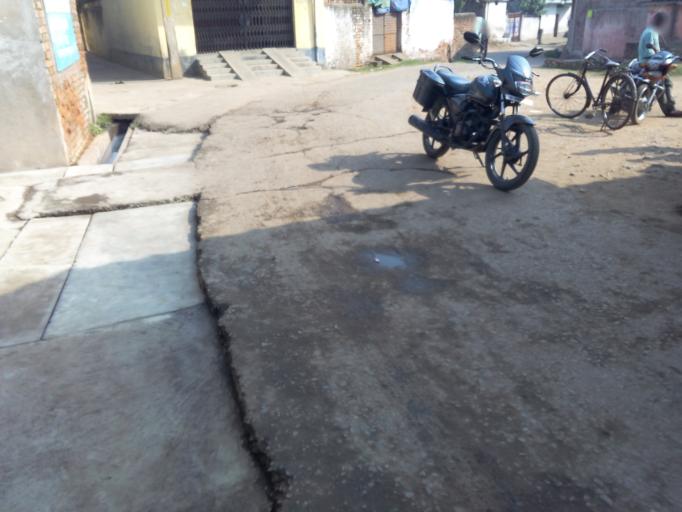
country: IN
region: Jharkhand
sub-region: Ramgarh
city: Barka Kana
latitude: 23.6647
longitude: 85.3264
